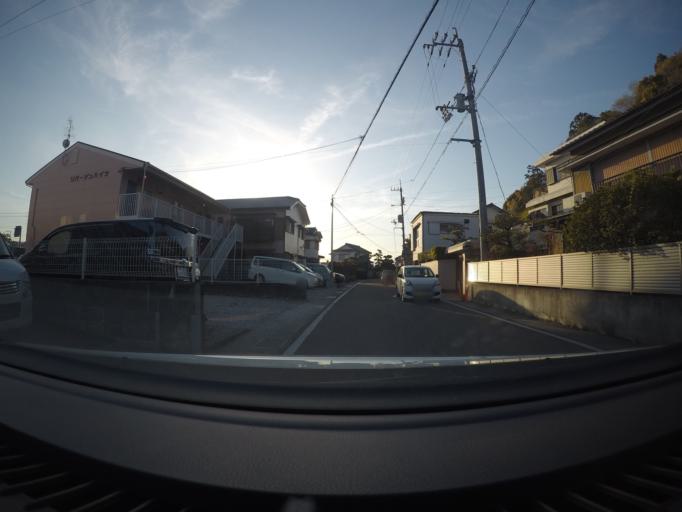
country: JP
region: Kochi
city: Kochi-shi
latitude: 33.5438
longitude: 133.5713
